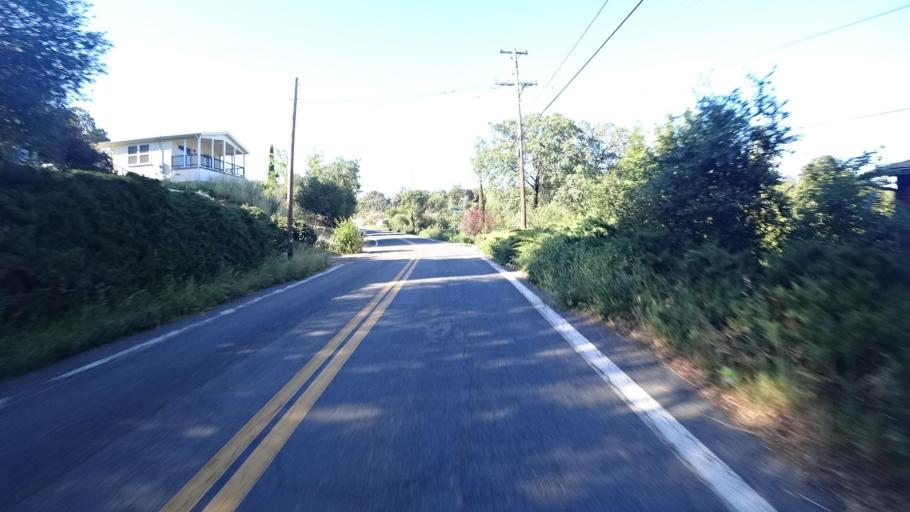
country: US
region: California
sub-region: Lake County
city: Nice
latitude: 39.1296
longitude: -122.8523
